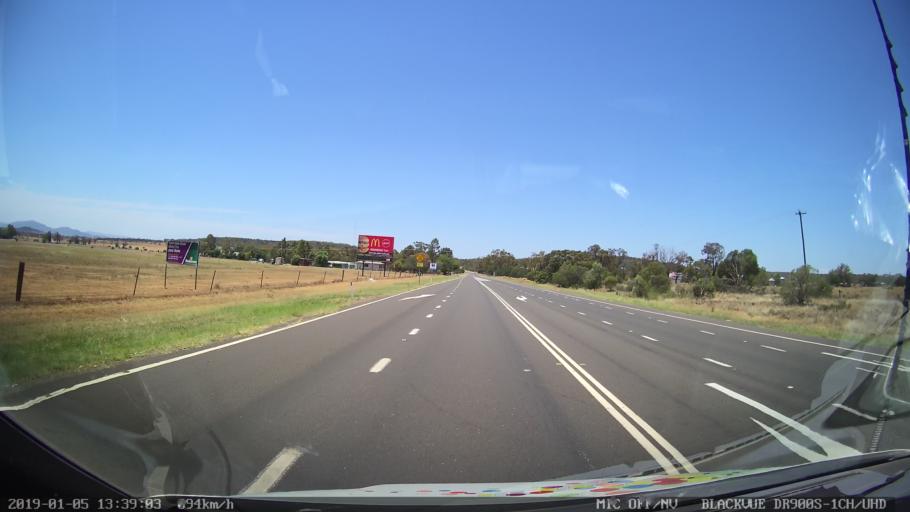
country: AU
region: New South Wales
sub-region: Gunnedah
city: Gunnedah
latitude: -30.9857
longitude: 150.2081
